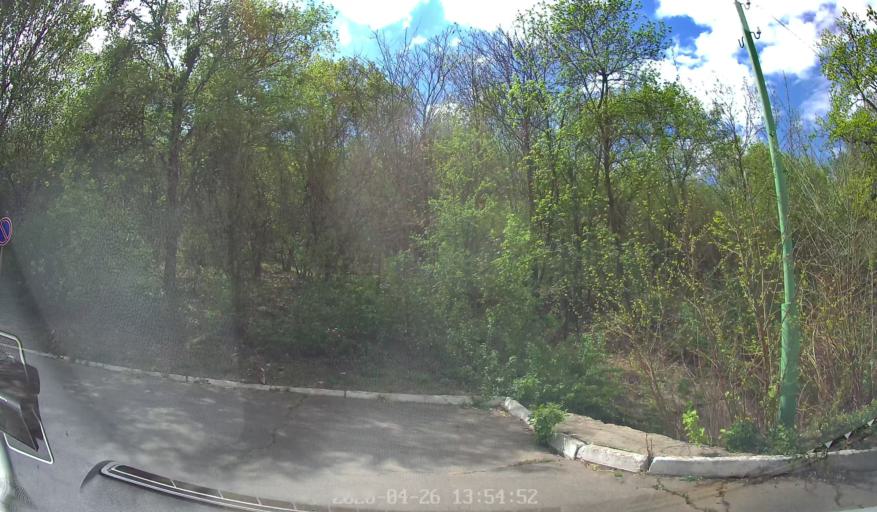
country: MD
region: Telenesti
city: Cocieri
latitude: 47.2873
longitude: 29.0992
